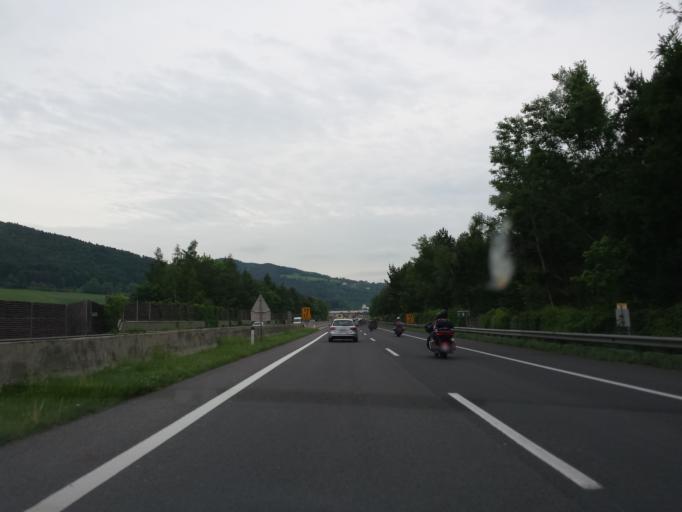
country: AT
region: Lower Austria
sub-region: Politischer Bezirk Neunkirchen
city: Warth
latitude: 47.6393
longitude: 16.1257
